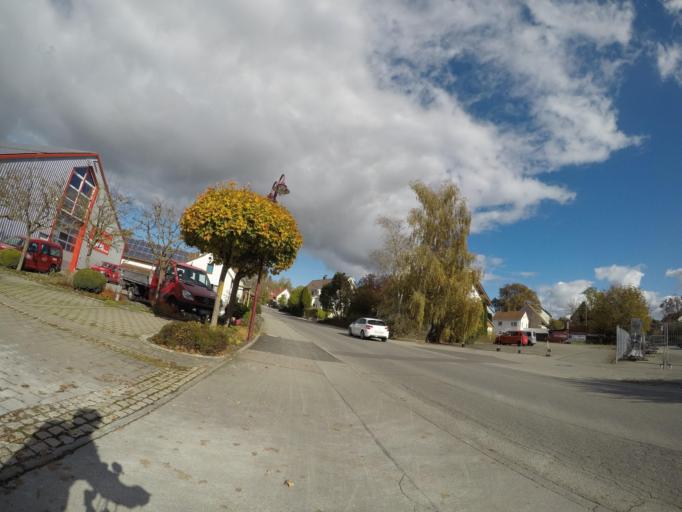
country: DE
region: Baden-Wuerttemberg
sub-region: Tuebingen Region
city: Oggelshausen
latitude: 48.0692
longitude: 9.6464
